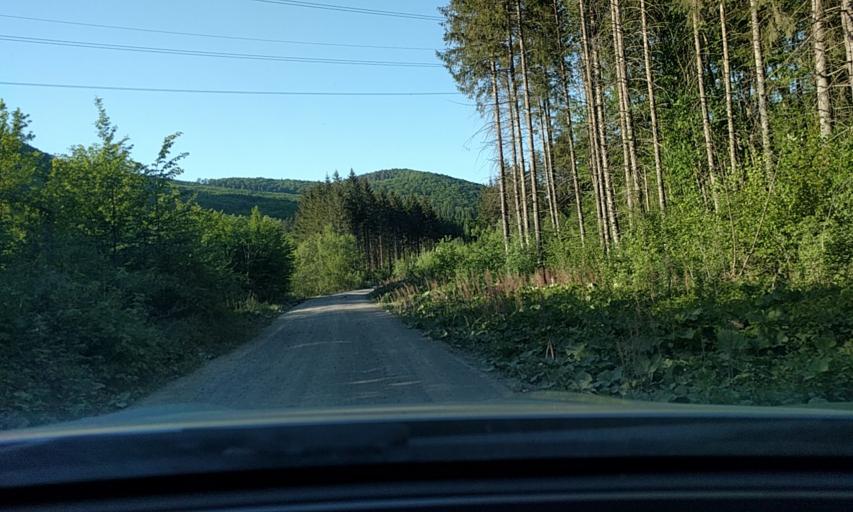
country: RO
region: Bacau
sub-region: Comuna Oituz
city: Ferestrau-Oituz
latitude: 46.1623
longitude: 26.5661
